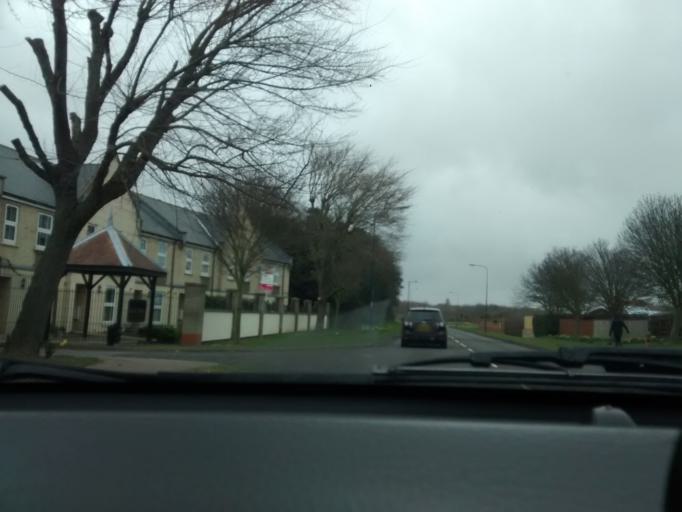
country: GB
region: England
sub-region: Suffolk
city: Felixstowe
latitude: 51.9697
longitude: 1.3471
